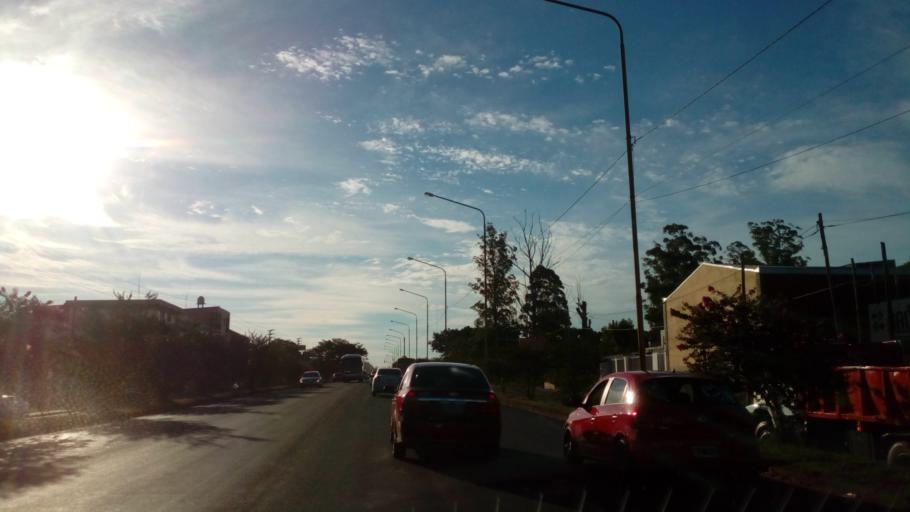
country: AR
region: Misiones
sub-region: Departamento de Capital
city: Posadas
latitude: -27.4039
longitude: -55.9074
